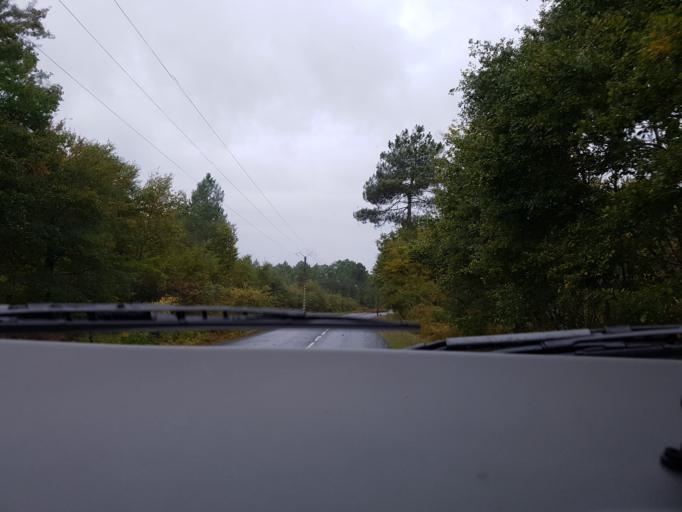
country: FR
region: Aquitaine
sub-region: Departement des Landes
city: Pissos
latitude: 44.3779
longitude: -0.6732
